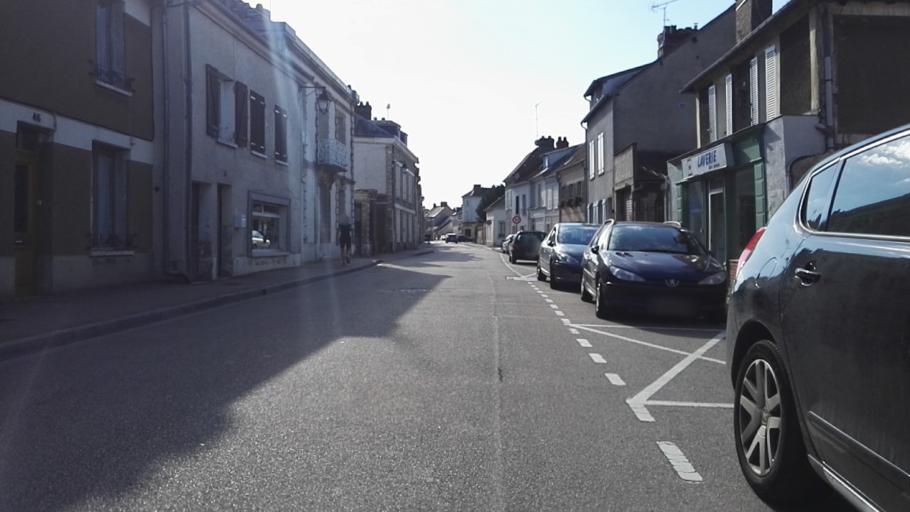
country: FR
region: Haute-Normandie
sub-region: Departement de l'Eure
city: Pacy-sur-Eure
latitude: 49.0160
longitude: 1.3777
